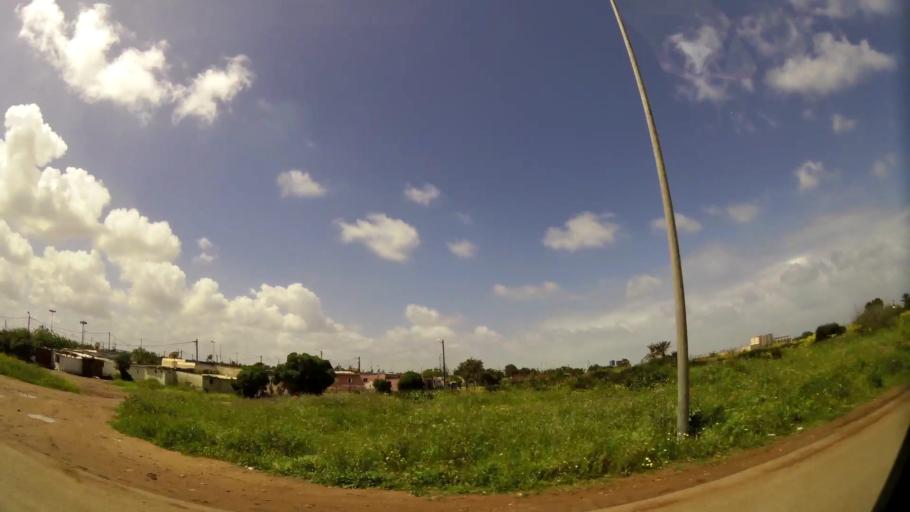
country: MA
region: Grand Casablanca
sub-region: Mediouna
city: Tit Mellil
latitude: 33.6356
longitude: -7.4594
